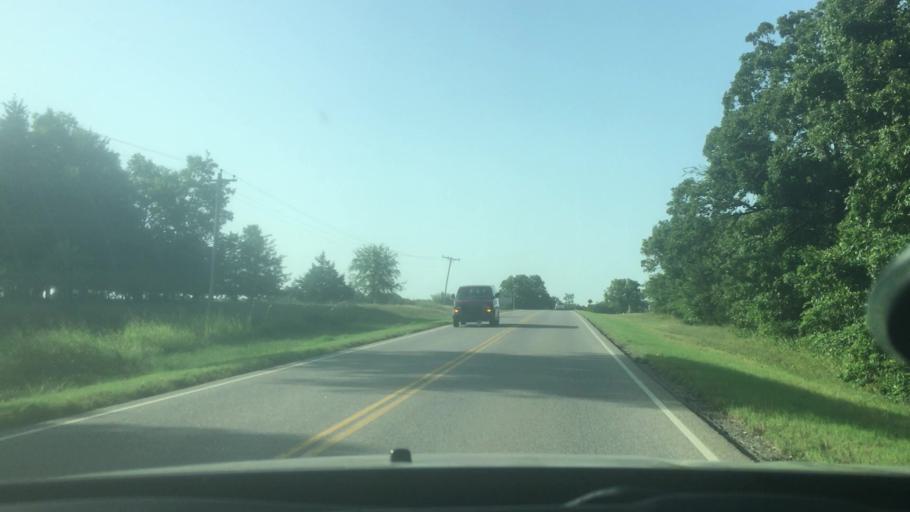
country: US
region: Oklahoma
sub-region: Bryan County
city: Durant
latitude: 34.1899
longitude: -96.4183
